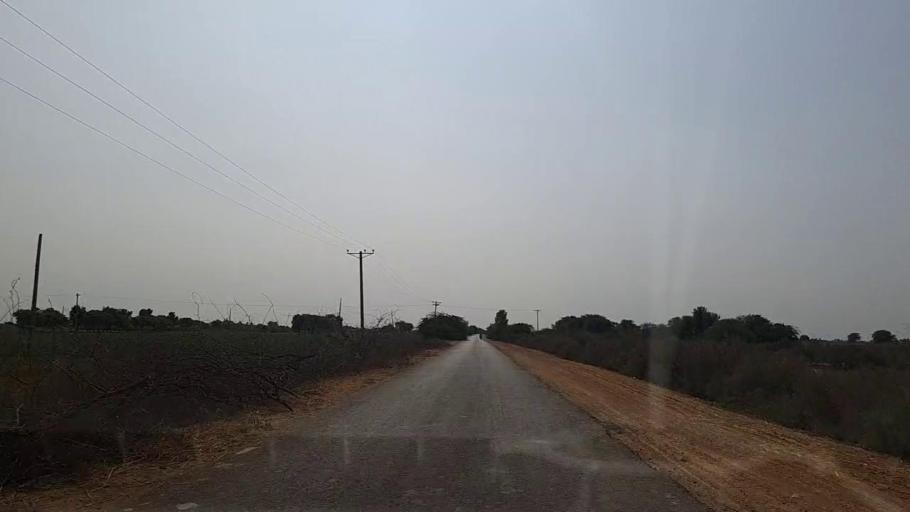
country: PK
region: Sindh
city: Chuhar Jamali
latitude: 24.3191
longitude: 67.9407
